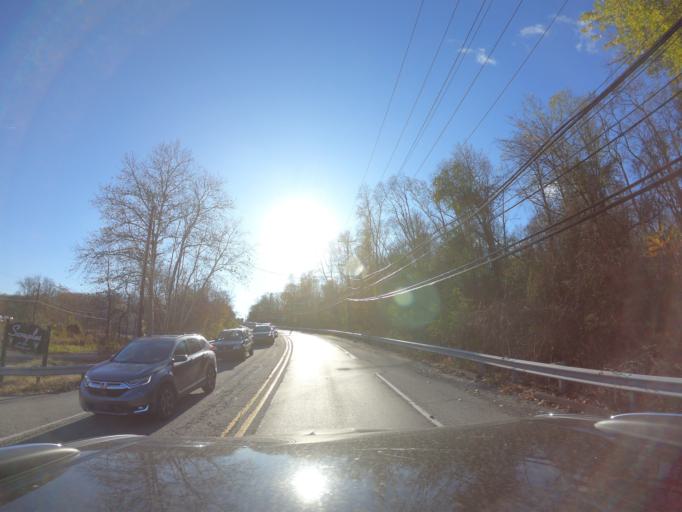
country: US
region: Pennsylvania
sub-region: Bucks County
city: Trevose
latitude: 40.1447
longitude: -74.9578
